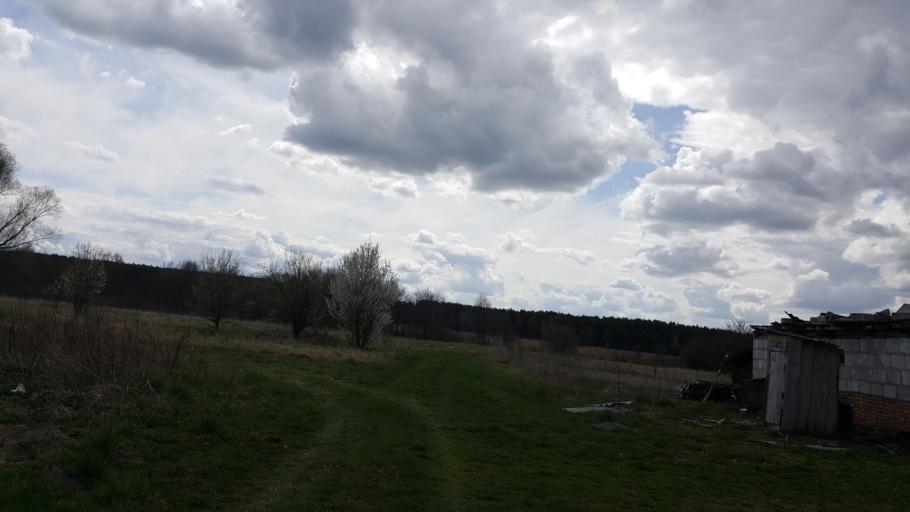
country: BY
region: Brest
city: Kamyanyets
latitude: 52.3500
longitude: 23.7104
